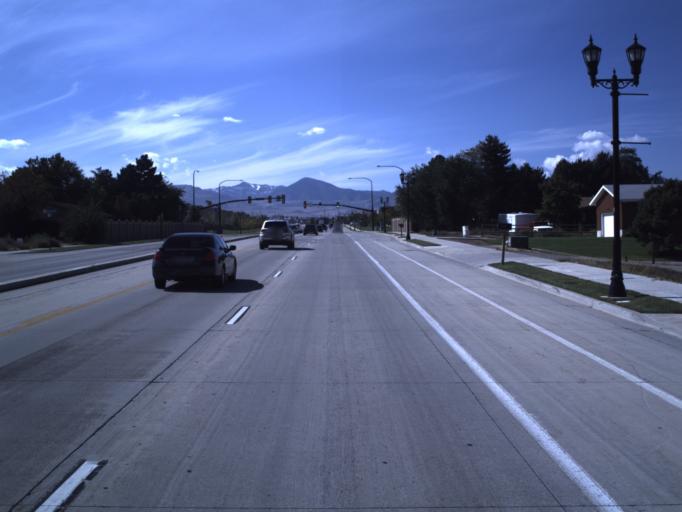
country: US
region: Utah
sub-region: Salt Lake County
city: South Jordan Heights
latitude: 40.5623
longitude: -111.9651
